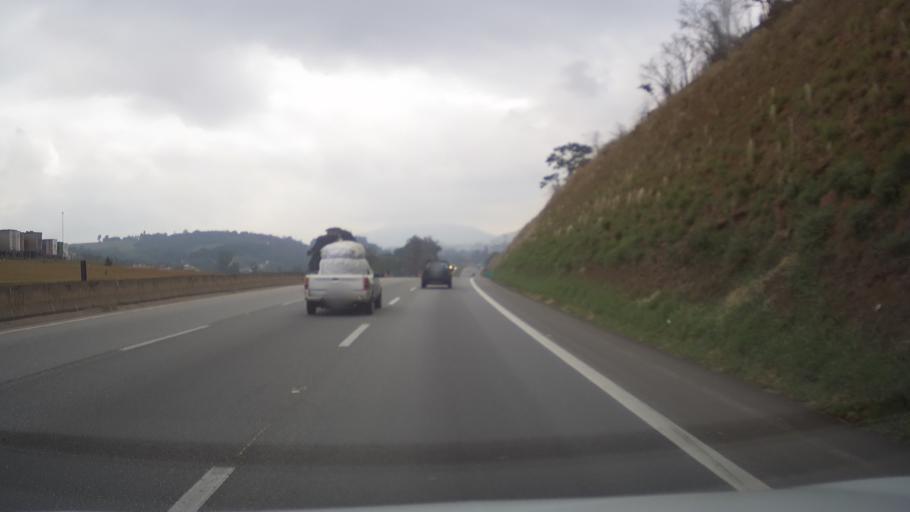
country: BR
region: Minas Gerais
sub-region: Extrema
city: Extrema
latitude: -22.8676
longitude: -46.3527
